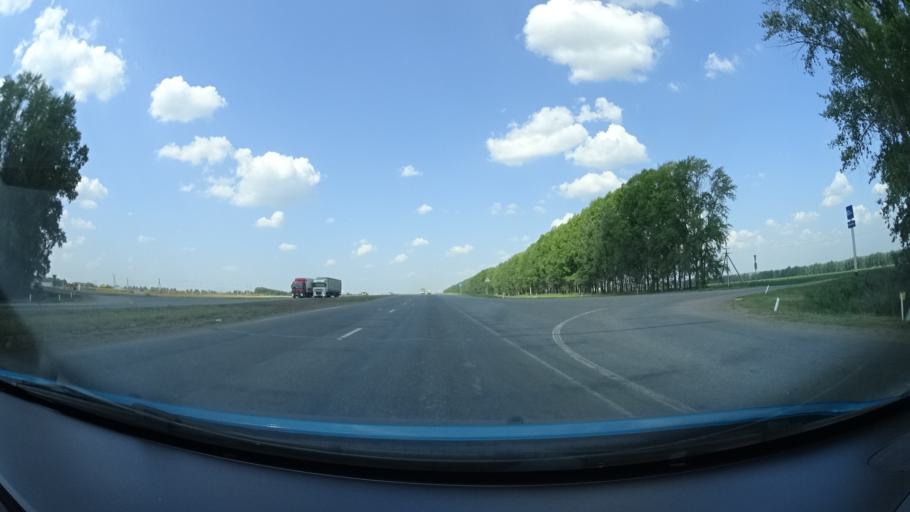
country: RU
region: Bashkortostan
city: Chishmy
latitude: 54.6549
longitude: 55.4873
